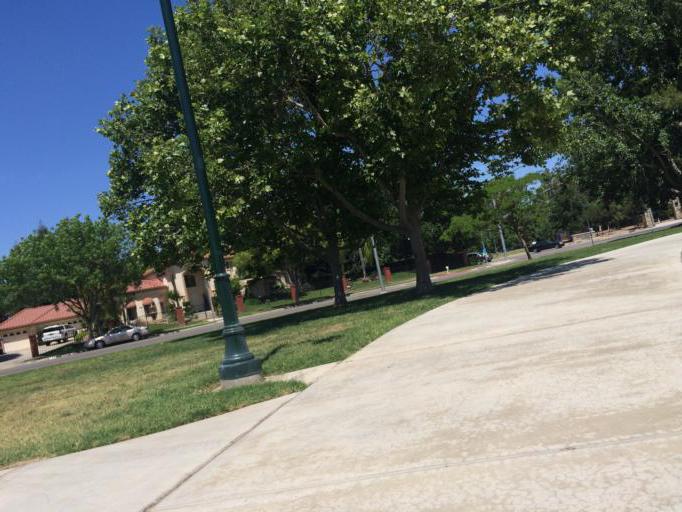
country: US
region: California
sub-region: Fresno County
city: Clovis
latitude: 36.8444
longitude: -119.7025
